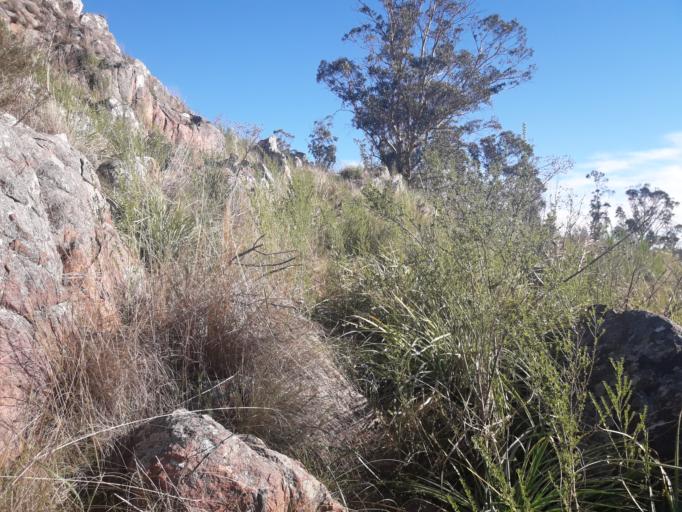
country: AR
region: Buenos Aires
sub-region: Partido de Tandil
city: Tandil
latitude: -37.3436
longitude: -59.1211
